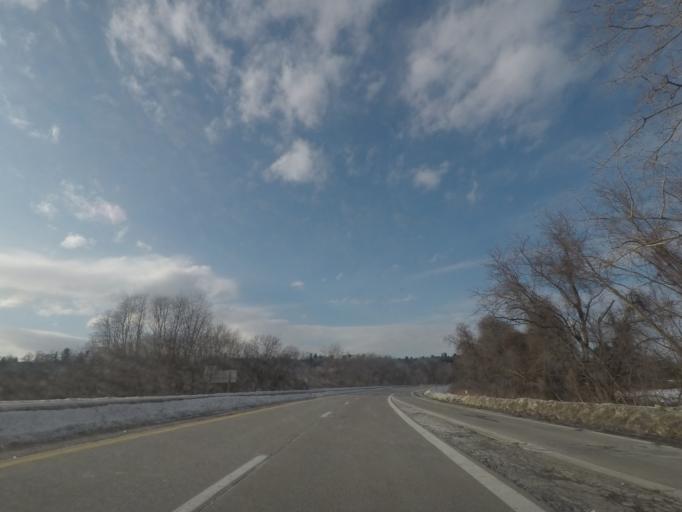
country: US
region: New York
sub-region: Schenectady County
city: Scotia
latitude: 42.8161
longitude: -73.9854
